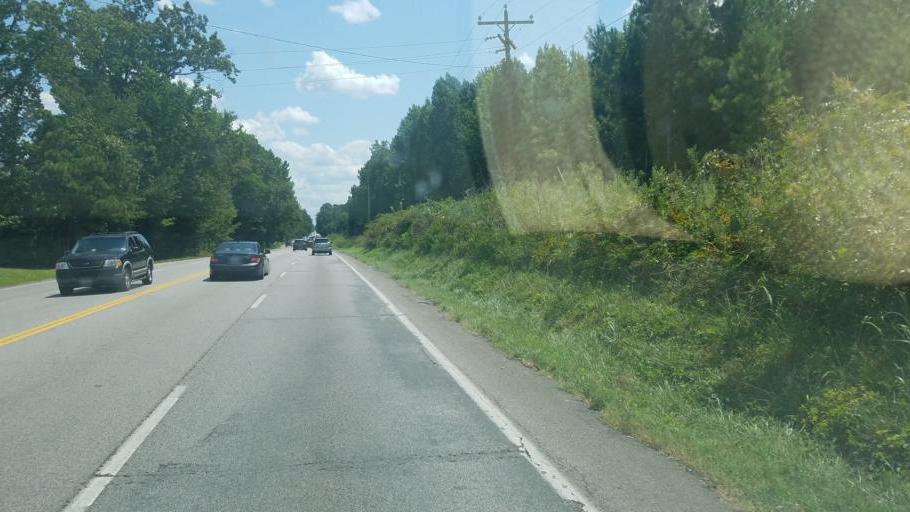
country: US
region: Virginia
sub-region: Prince George County
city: Prince George
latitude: 37.1366
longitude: -77.2455
